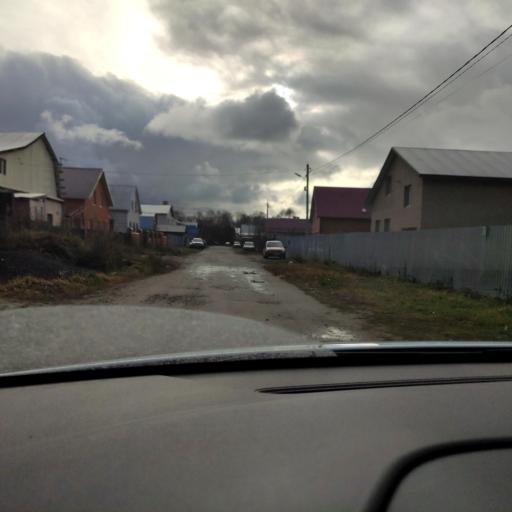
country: RU
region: Tatarstan
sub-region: Gorod Kazan'
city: Kazan
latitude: 55.8829
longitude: 49.0993
